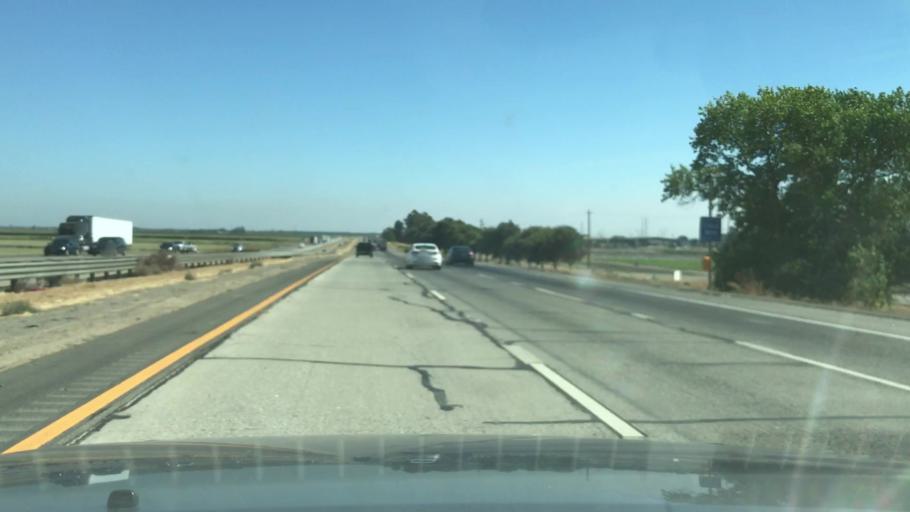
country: US
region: California
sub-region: San Joaquin County
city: Woodbridge
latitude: 38.0950
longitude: -121.3860
